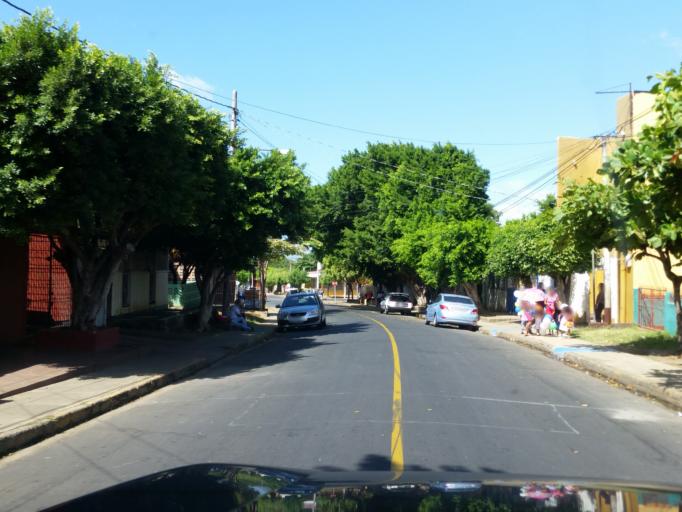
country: NI
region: Managua
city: Managua
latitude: 12.1176
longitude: -86.2374
